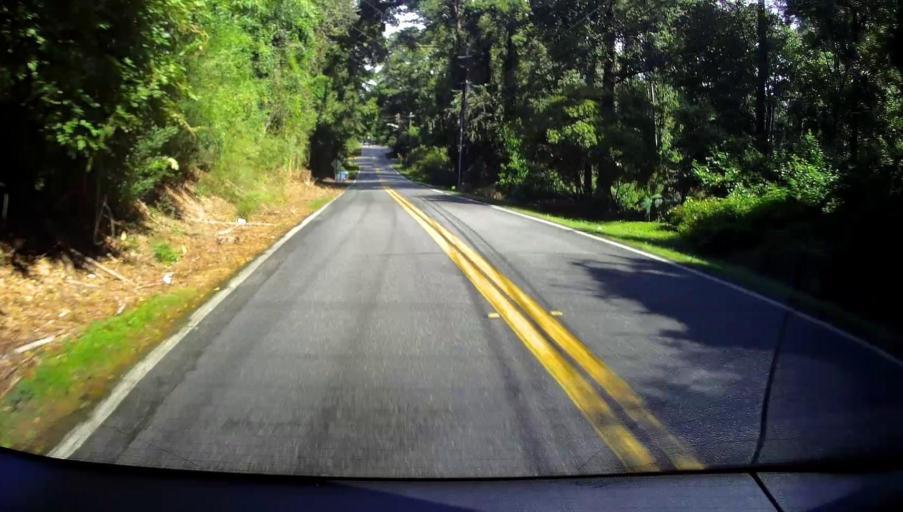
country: US
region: Georgia
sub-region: Bibb County
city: Macon
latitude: 32.8863
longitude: -83.7174
